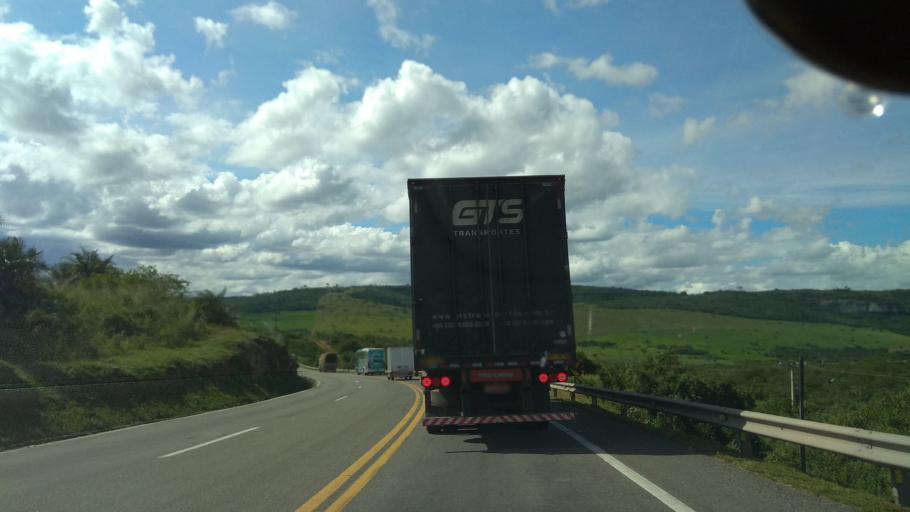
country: BR
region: Bahia
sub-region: Santa Ines
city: Santa Ines
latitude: -13.1738
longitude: -39.9995
